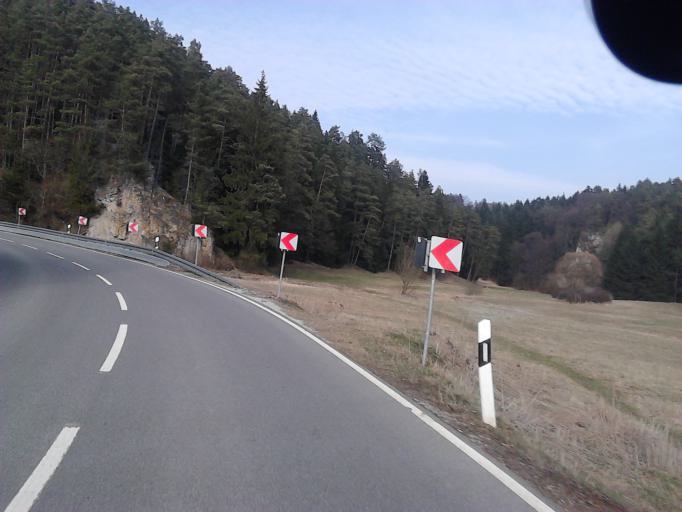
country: DE
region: Bavaria
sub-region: Upper Franconia
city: Stadelhofen
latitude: 49.9723
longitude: 11.1908
